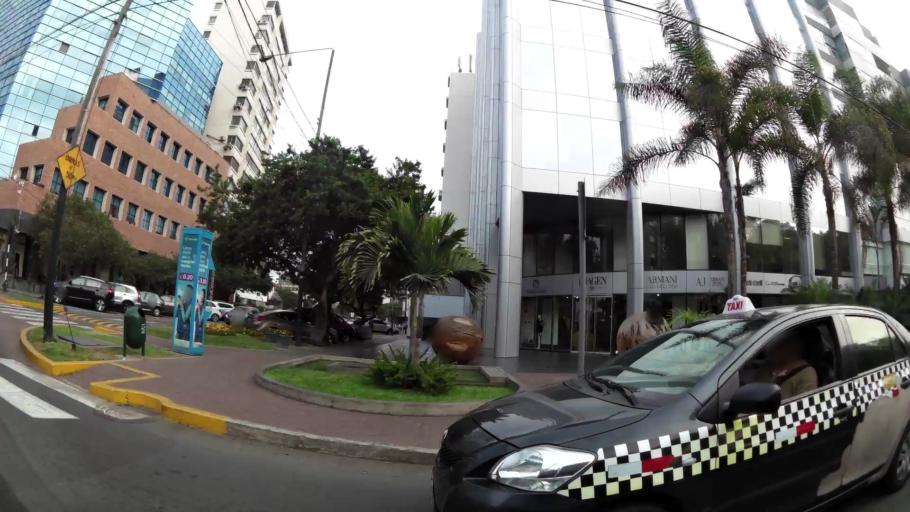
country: PE
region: Lima
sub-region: Lima
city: San Isidro
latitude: -12.1055
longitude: -77.0404
